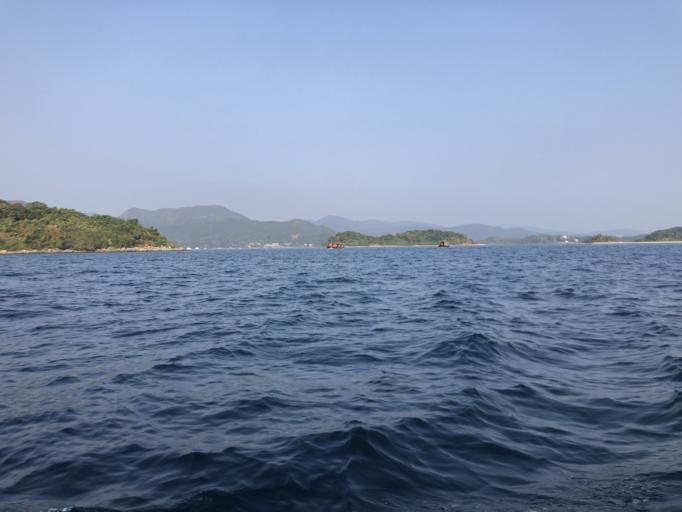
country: HK
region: Sai Kung
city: Sai Kung
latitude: 22.3765
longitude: 114.2796
